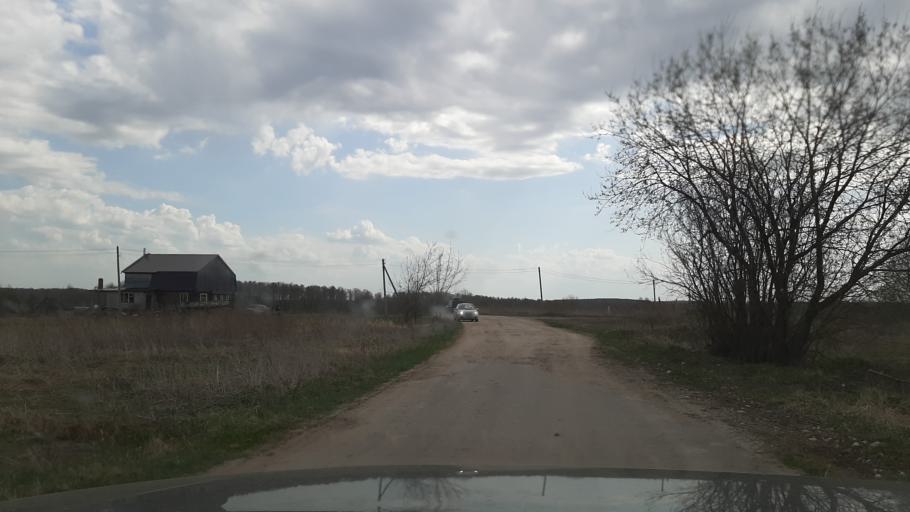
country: RU
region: Ivanovo
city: Furmanov
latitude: 57.3188
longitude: 41.1564
